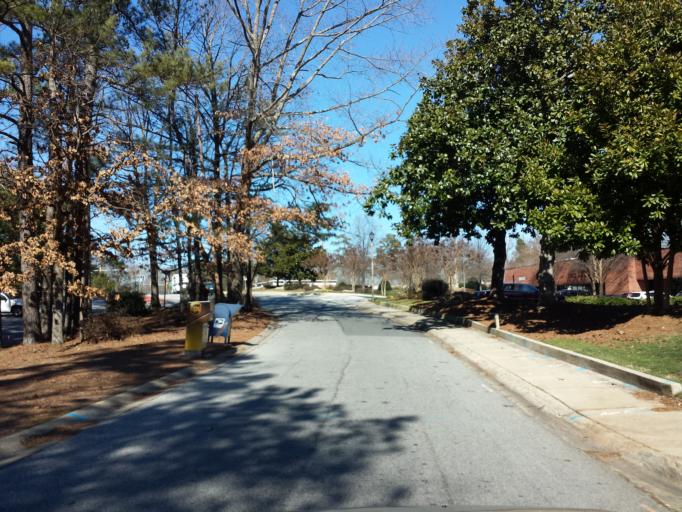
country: US
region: Georgia
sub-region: Cobb County
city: Vinings
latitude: 33.9011
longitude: -84.4541
